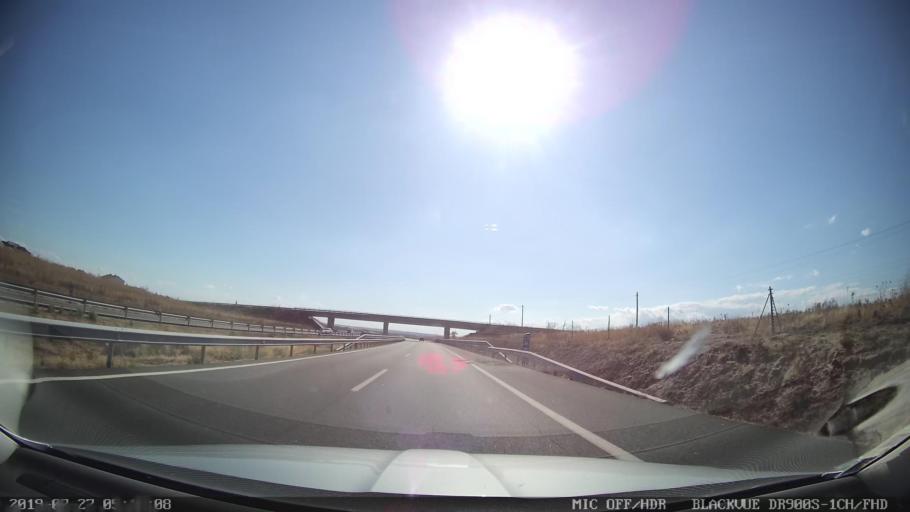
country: ES
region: Castille-La Mancha
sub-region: Province of Toledo
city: Santa Olalla
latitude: 40.0350
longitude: -4.4274
